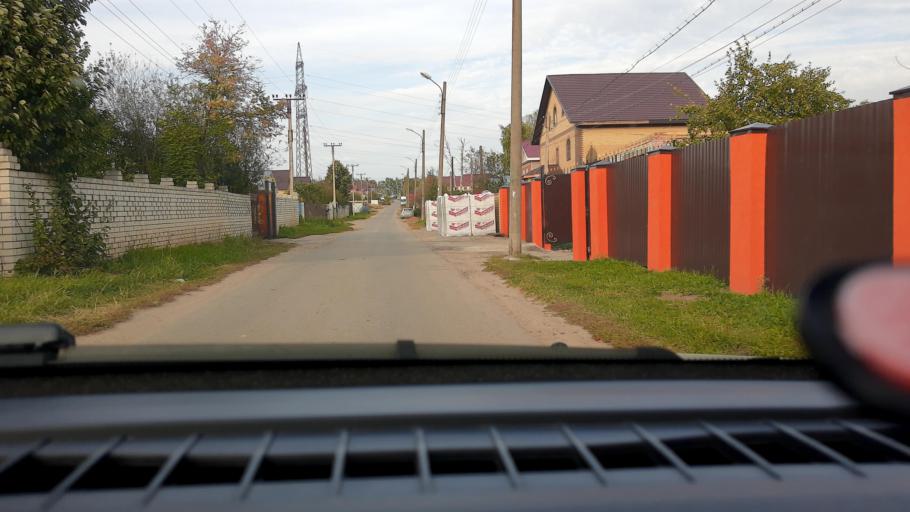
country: RU
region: Nizjnij Novgorod
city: Nizhniy Novgorod
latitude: 56.2097
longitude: 43.9552
